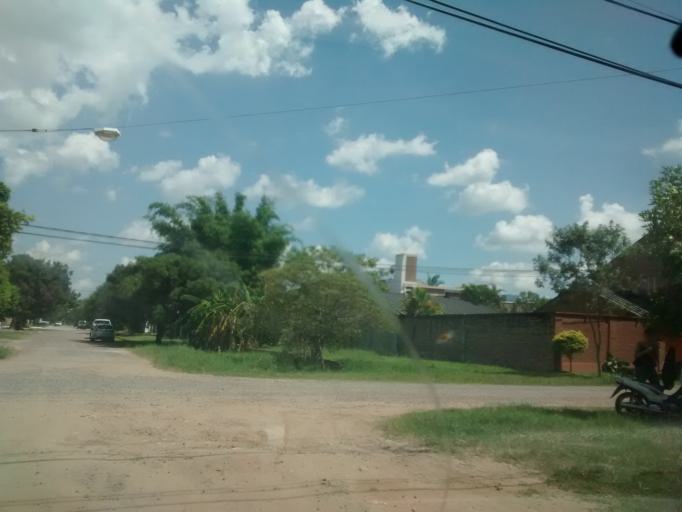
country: AR
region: Chaco
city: Resistencia
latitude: -27.4392
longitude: -58.9695
